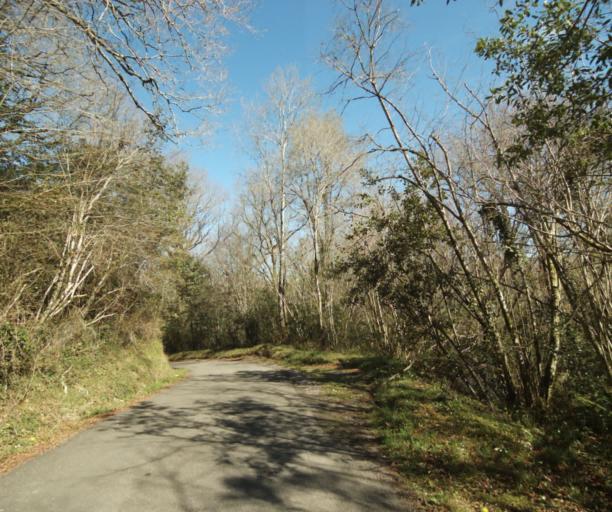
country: FR
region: Aquitaine
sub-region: Departement des Pyrenees-Atlantiques
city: Ciboure
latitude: 43.3657
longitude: -1.6722
